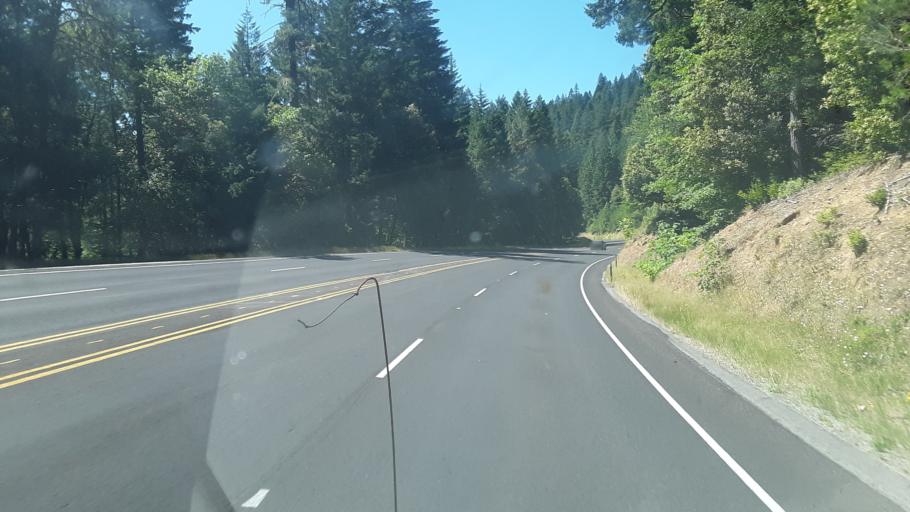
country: US
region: Oregon
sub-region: Josephine County
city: Cave Junction
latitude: 41.9149
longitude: -123.7687
